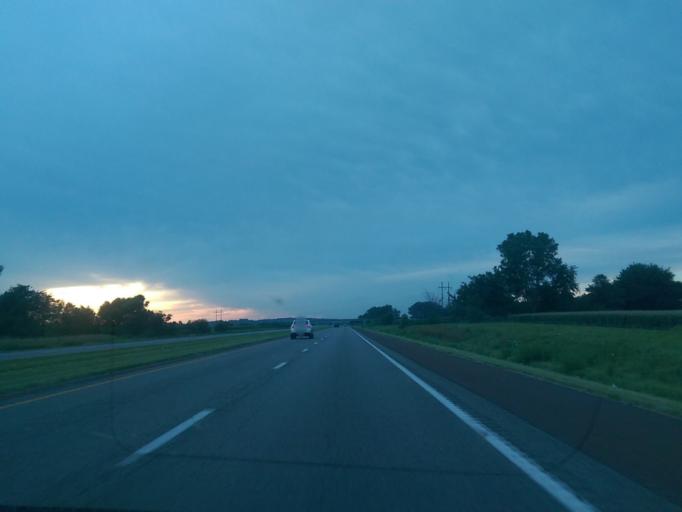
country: US
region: Missouri
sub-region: Holt County
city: Mound City
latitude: 40.1755
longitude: -95.3064
